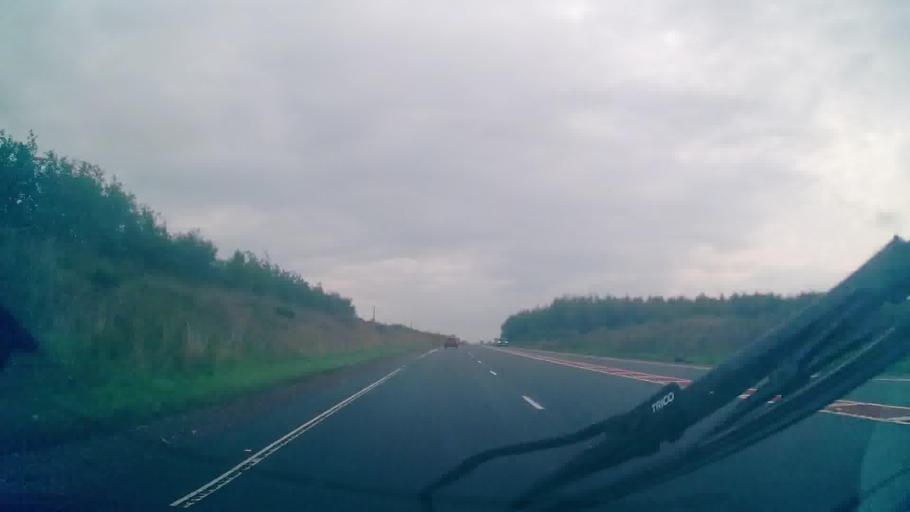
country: GB
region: Scotland
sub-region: Dumfries and Galloway
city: Lockerbie
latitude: 55.0238
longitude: -3.3773
